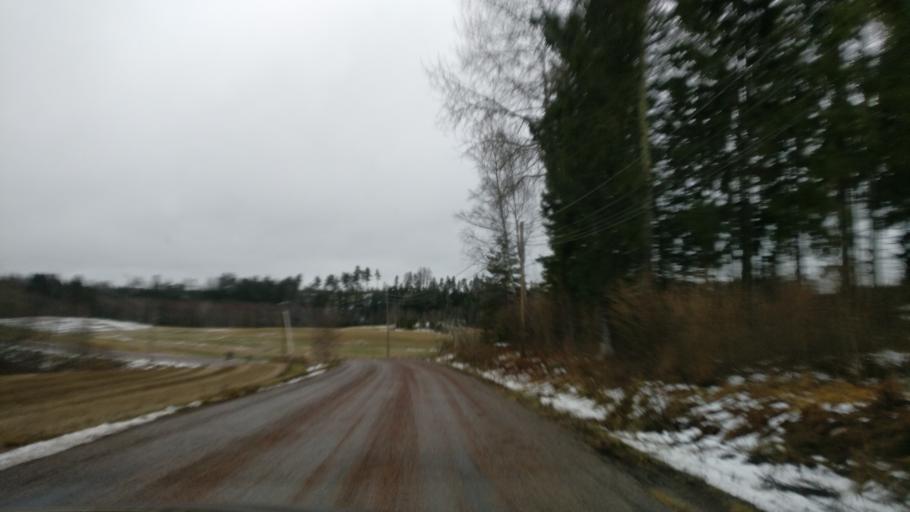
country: FI
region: Uusimaa
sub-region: Raaseporin
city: Karis
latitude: 60.0845
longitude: 23.7792
